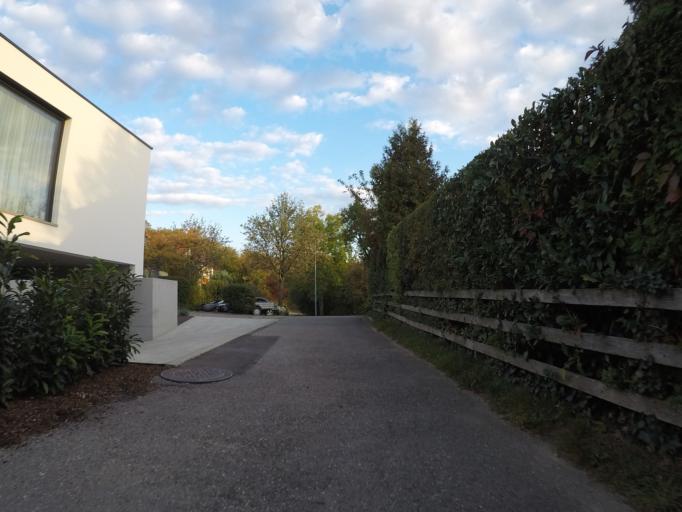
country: DE
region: Baden-Wuerttemberg
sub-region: Tuebingen Region
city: Eningen unter Achalm
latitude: 48.4883
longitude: 9.2478
